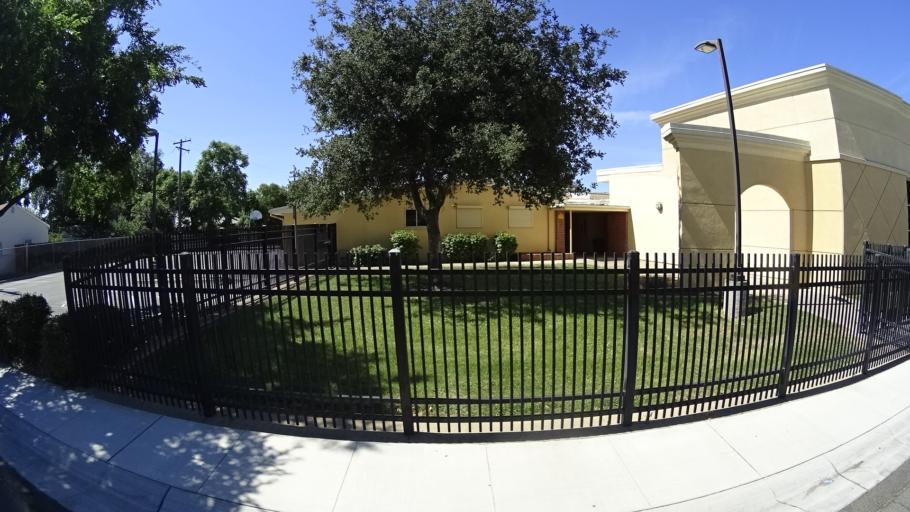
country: US
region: California
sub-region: Sacramento County
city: Parkway
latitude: 38.5188
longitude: -121.5034
